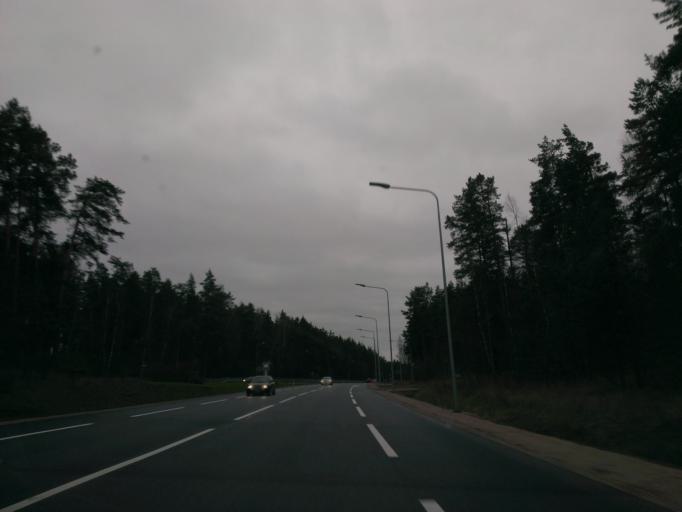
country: LV
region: Adazi
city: Adazi
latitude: 57.0607
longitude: 24.3220
